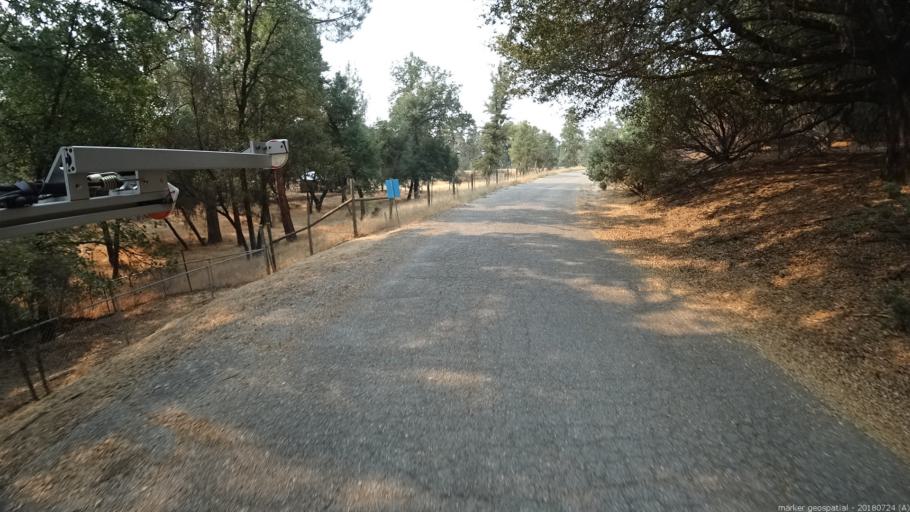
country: US
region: California
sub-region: Madera County
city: Oakhurst
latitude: 37.3093
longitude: -119.6235
